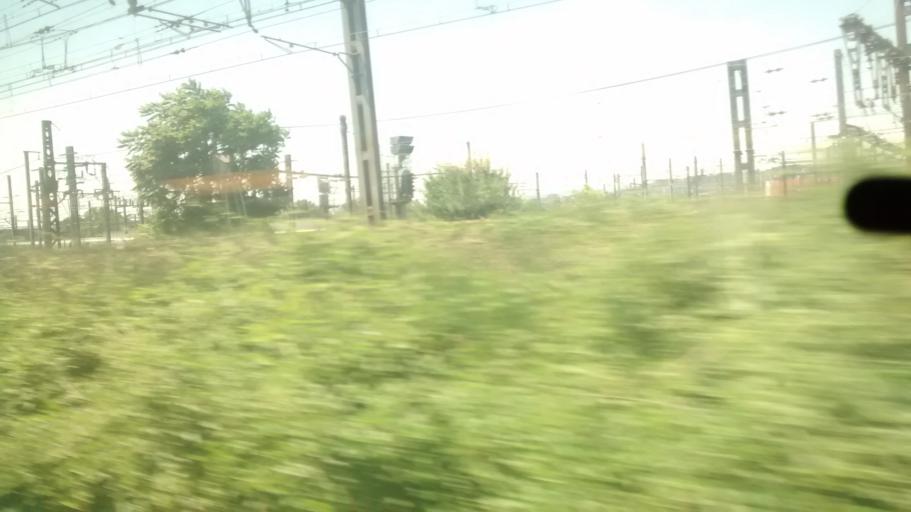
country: FR
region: Rhone-Alpes
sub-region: Departement du Rhone
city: Lyon
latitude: 45.7307
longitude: 4.8493
